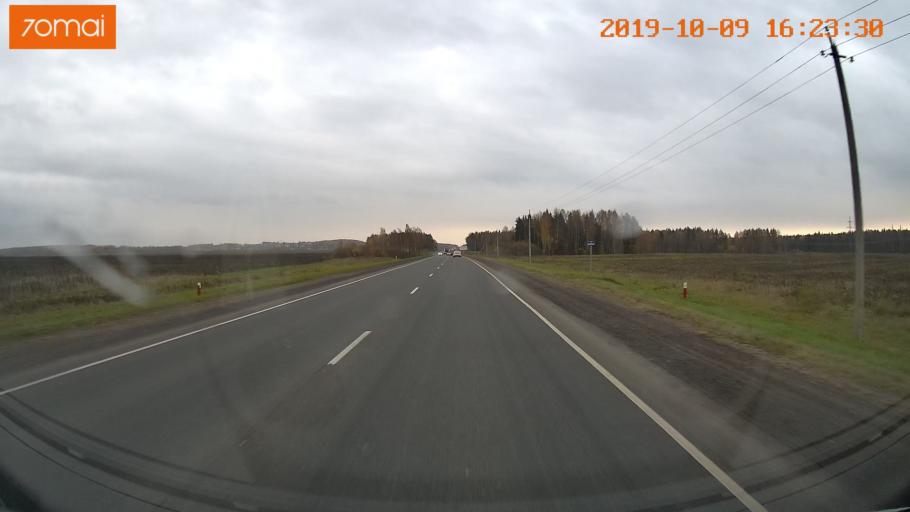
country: RU
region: Kostroma
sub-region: Kostromskoy Rayon
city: Kostroma
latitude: 57.6635
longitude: 40.8998
